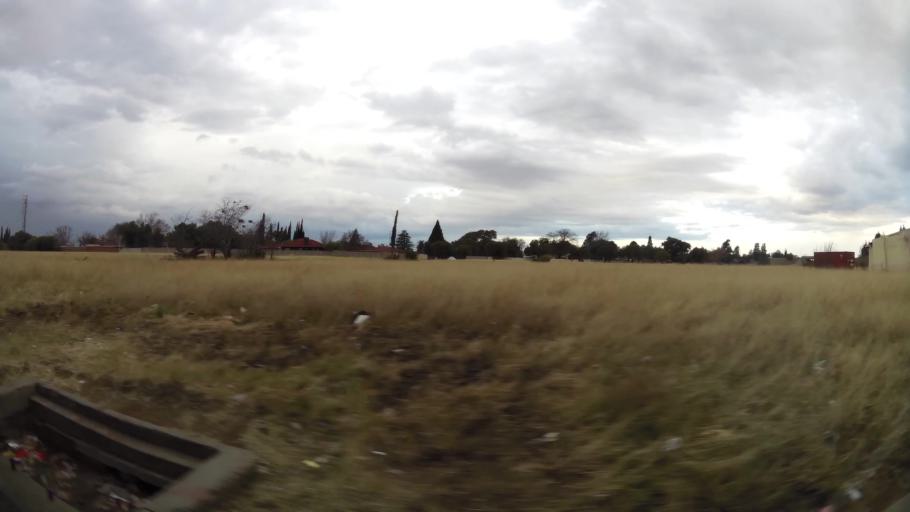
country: ZA
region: Orange Free State
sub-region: Lejweleputswa District Municipality
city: Welkom
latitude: -27.9567
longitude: 26.7236
